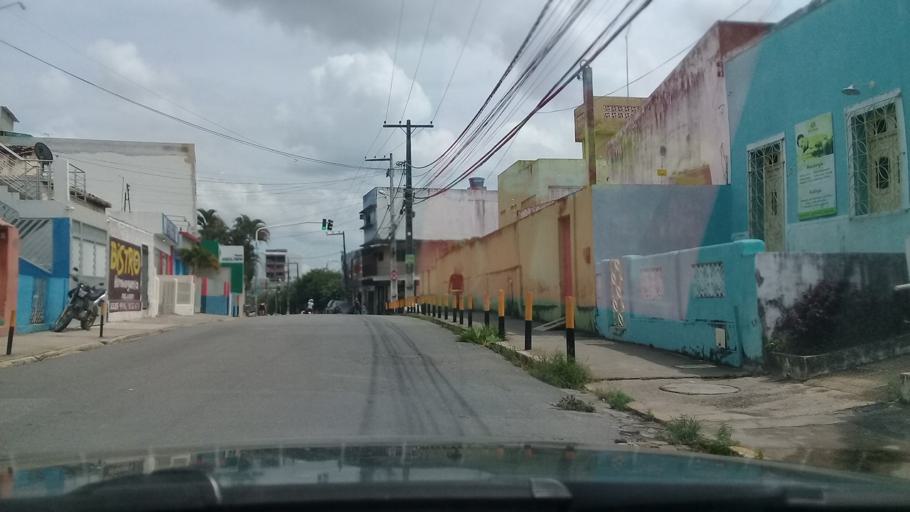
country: BR
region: Pernambuco
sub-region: Vitoria De Santo Antao
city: Vitoria de Santo Antao
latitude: -8.1141
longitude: -35.2908
